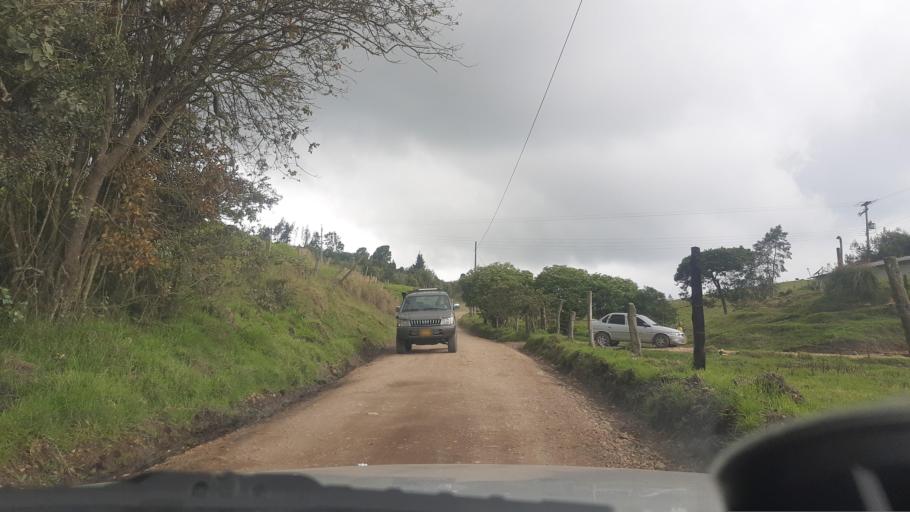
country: CO
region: Cundinamarca
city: Suesca
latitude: 5.1429
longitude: -73.7788
